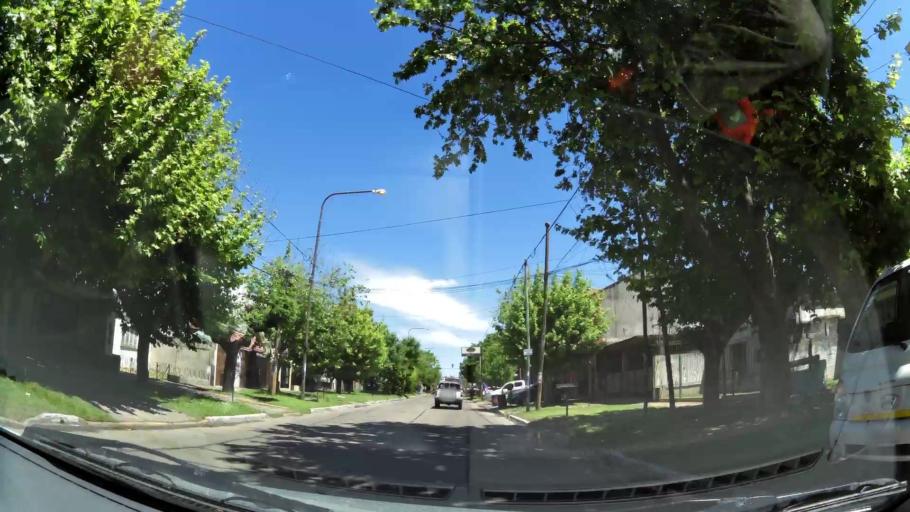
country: AR
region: Buenos Aires
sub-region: Partido de Quilmes
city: Quilmes
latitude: -34.7307
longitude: -58.2752
